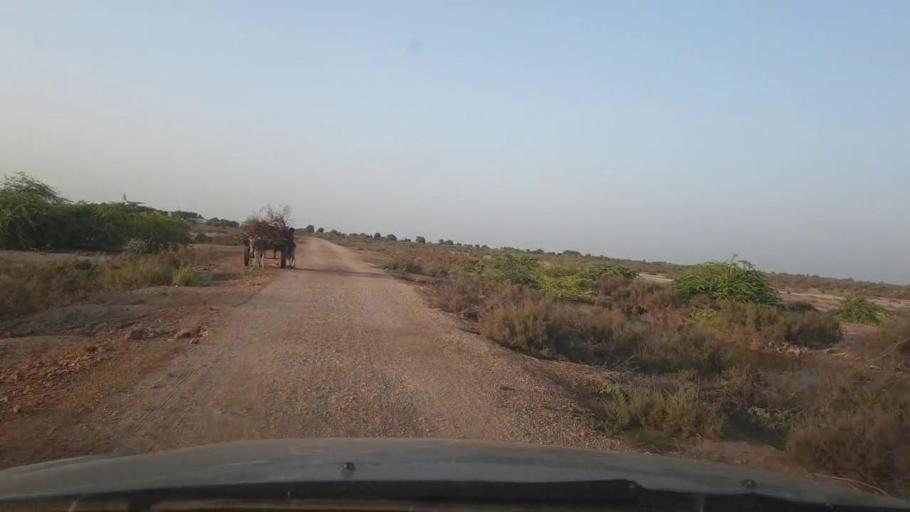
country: PK
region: Sindh
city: Tando Ghulam Ali
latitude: 25.1693
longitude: 68.9763
